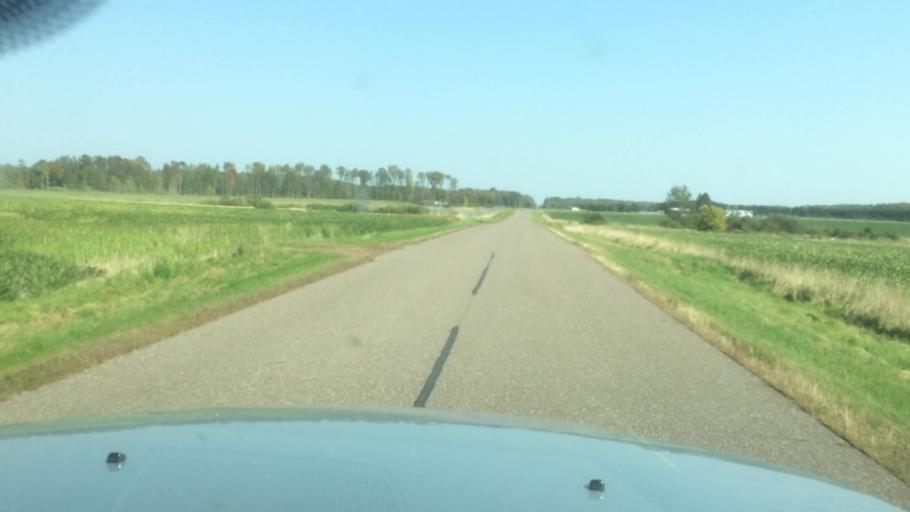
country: US
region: Wisconsin
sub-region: Taylor County
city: Medford
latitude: 45.0914
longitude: -90.3069
